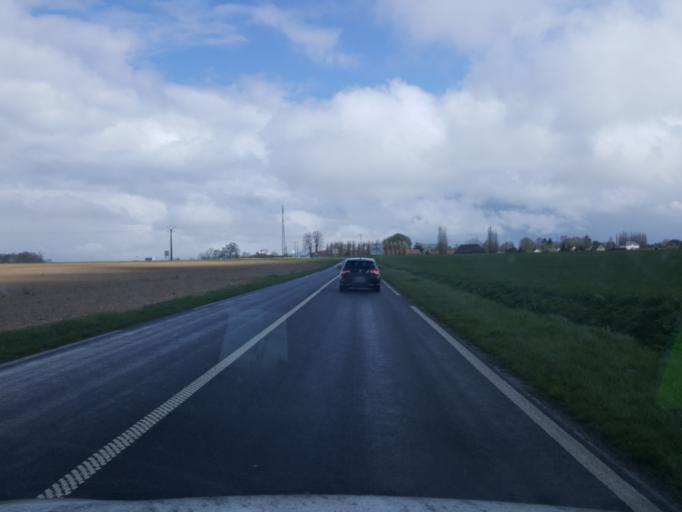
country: FR
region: Picardie
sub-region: Departement de l'Oise
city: Auneuil
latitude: 49.3619
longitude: 1.9688
